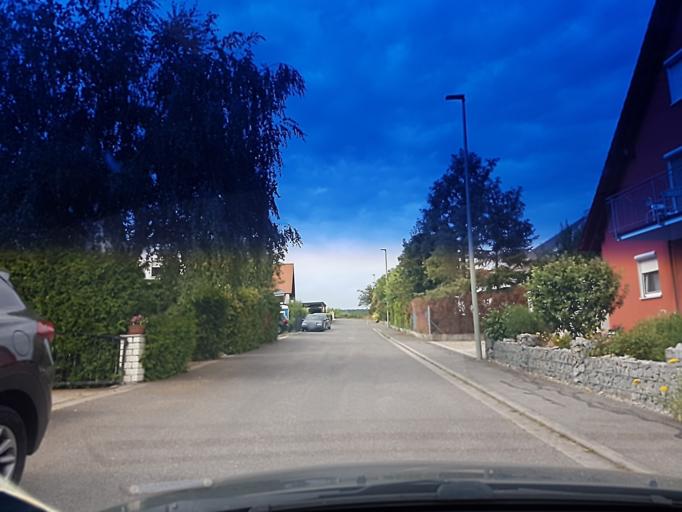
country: DE
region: Bavaria
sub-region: Upper Franconia
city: Frensdorf
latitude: 49.8252
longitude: 10.8826
